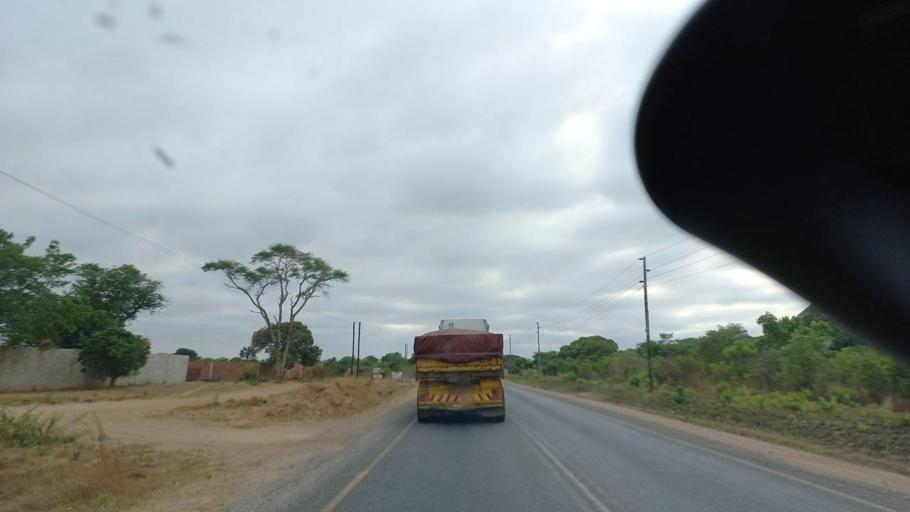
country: ZM
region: Lusaka
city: Chongwe
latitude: -15.3530
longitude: 28.5488
